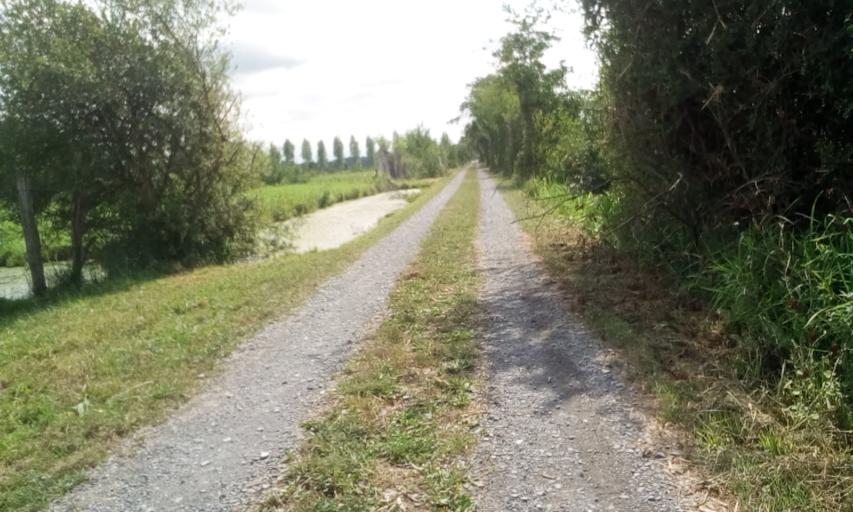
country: FR
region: Lower Normandy
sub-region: Departement du Calvados
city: Bavent
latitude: 49.2300
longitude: -0.1697
